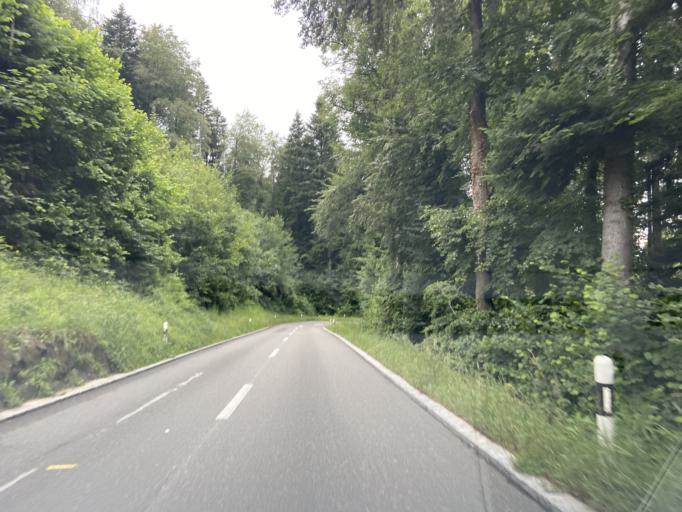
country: CH
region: Thurgau
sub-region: Muenchwilen District
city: Aadorf
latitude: 47.4641
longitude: 8.8929
